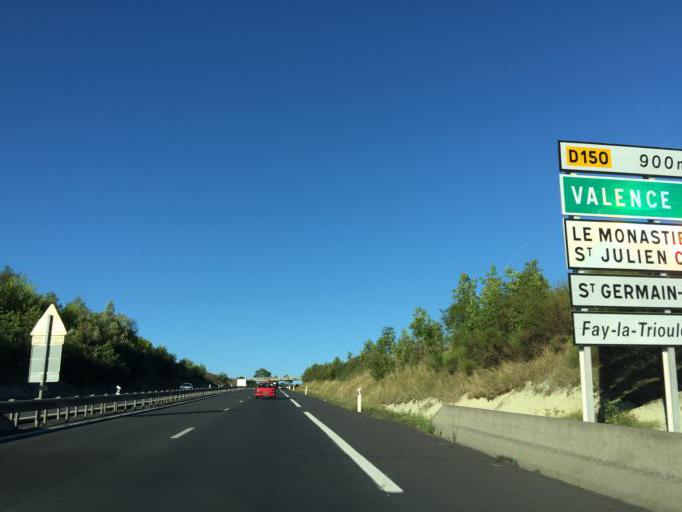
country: FR
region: Auvergne
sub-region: Departement de la Haute-Loire
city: Brives-Charensac
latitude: 45.0572
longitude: 3.9295
